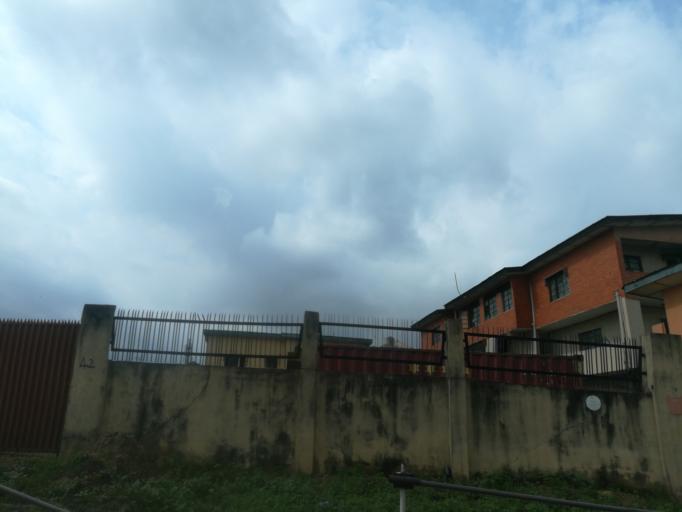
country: NG
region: Lagos
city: Ikeja
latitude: 6.6234
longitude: 3.3559
